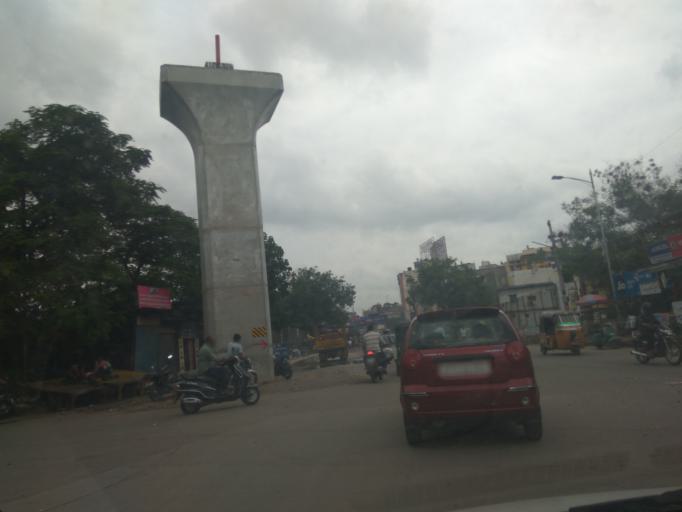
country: IN
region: Telangana
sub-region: Hyderabad
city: Hyderabad
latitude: 17.3995
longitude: 78.4947
